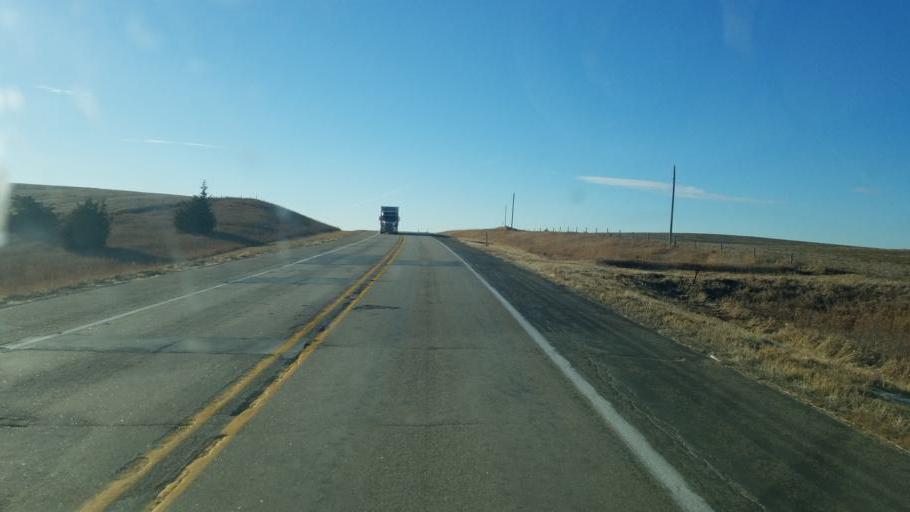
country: US
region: Nebraska
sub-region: Dixon County
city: Ponca
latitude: 42.4740
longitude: -96.7869
